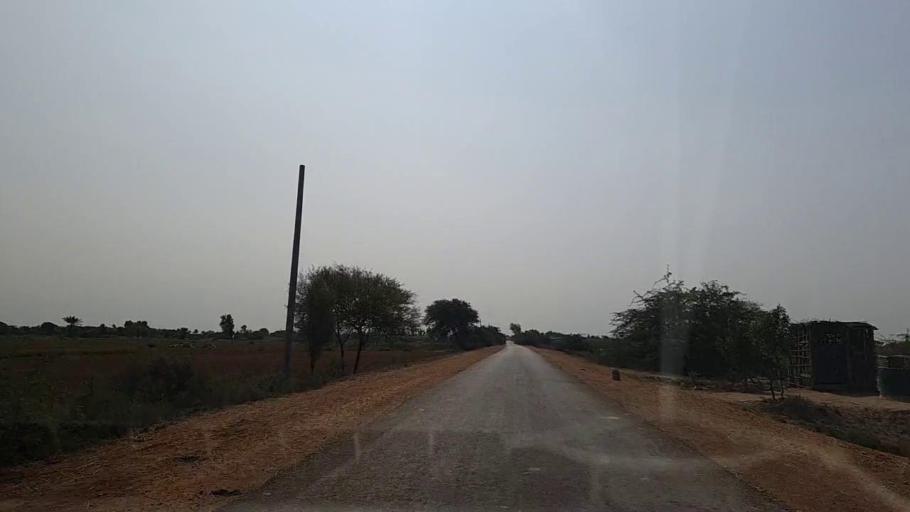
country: PK
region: Sindh
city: Chuhar Jamali
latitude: 24.3154
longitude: 67.9399
